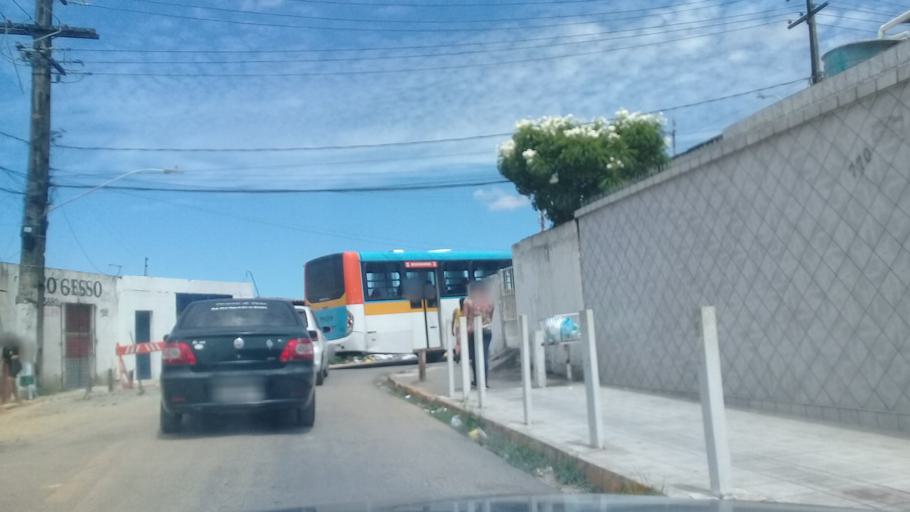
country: BR
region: Pernambuco
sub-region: Jaboatao Dos Guararapes
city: Jaboatao dos Guararapes
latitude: -8.1218
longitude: -34.9538
